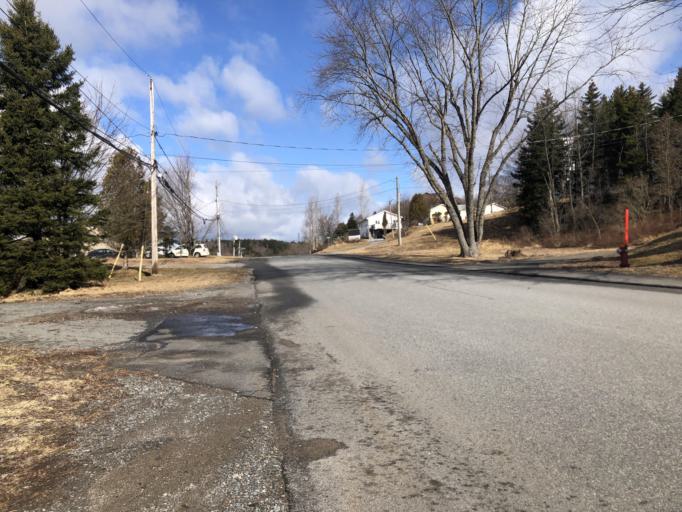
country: CA
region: New Brunswick
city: Saint John
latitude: 45.3190
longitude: -66.0089
